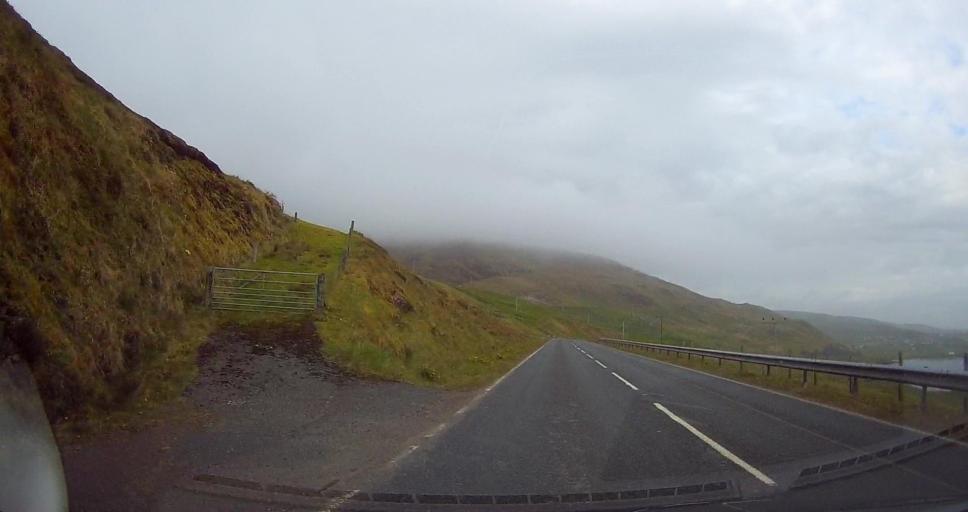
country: GB
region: Scotland
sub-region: Shetland Islands
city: Sandwick
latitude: 60.0213
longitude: -1.2337
